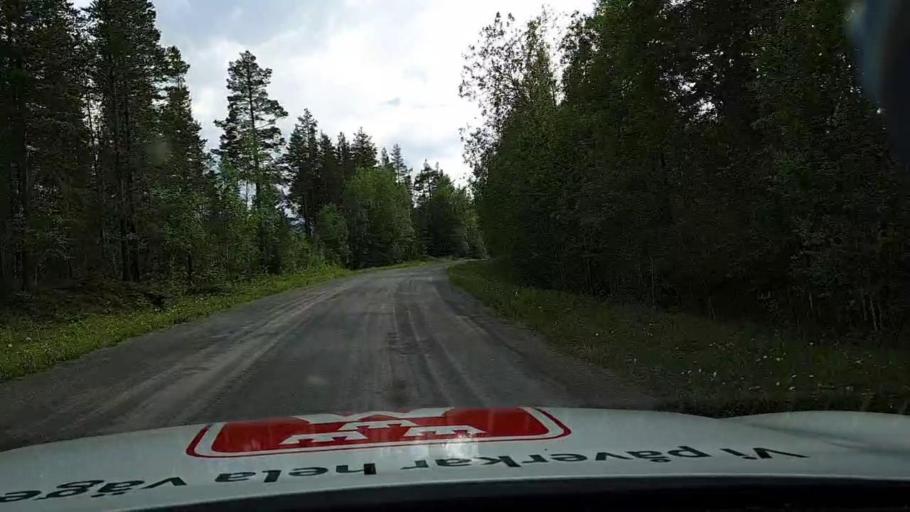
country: SE
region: Jaemtland
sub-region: OEstersunds Kommun
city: Brunflo
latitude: 63.1196
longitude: 15.0908
